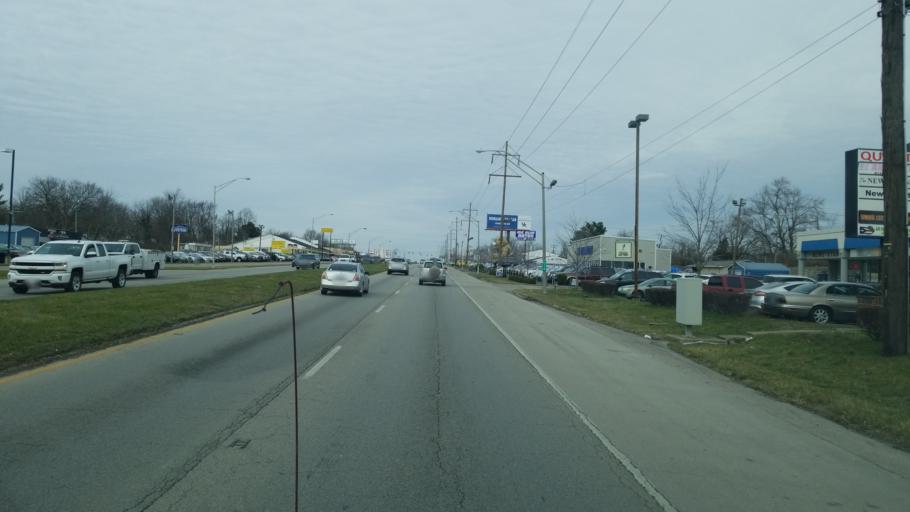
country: US
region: Kentucky
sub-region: Fayette County
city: Lexington-Fayette
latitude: 38.0525
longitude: -84.4575
